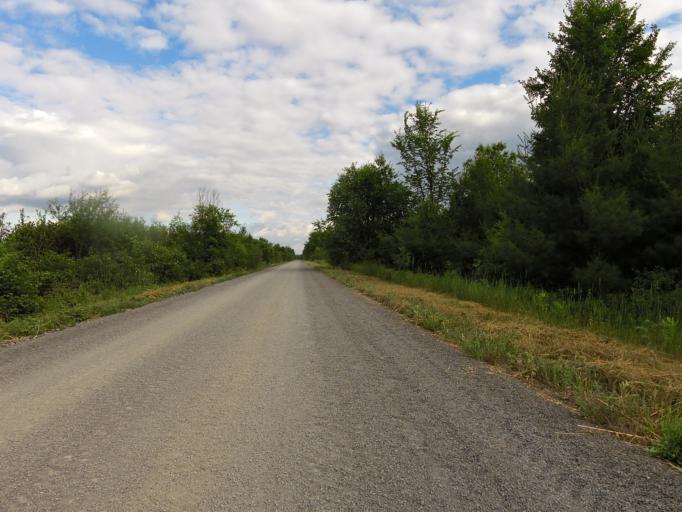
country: CA
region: Ontario
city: Arnprior
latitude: 45.2935
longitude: -76.2586
